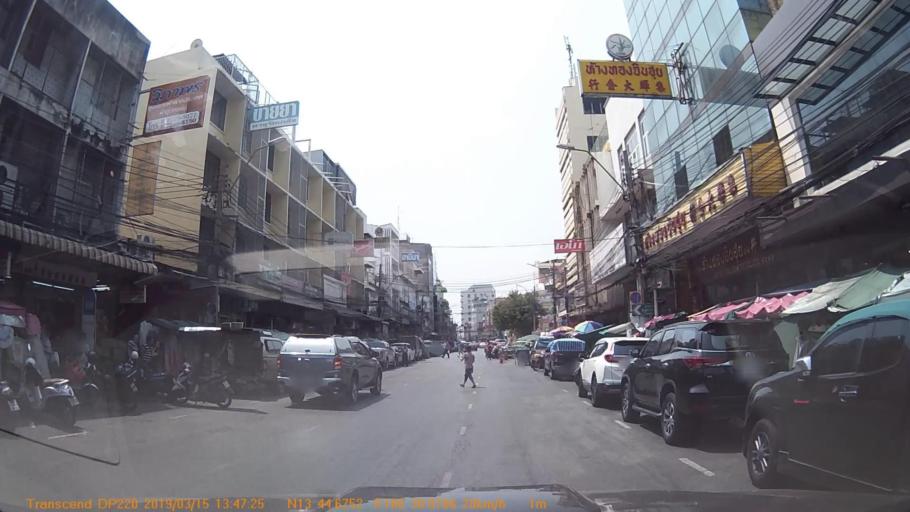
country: TH
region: Bangkok
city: Bangkok
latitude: 13.7446
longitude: 100.5012
